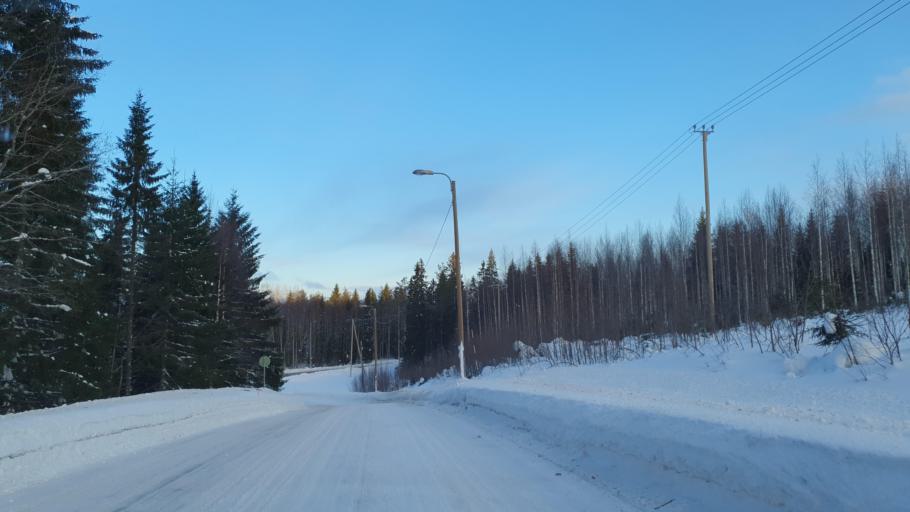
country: FI
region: Kainuu
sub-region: Kajaani
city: Ristijaervi
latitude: 64.3394
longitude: 28.0577
